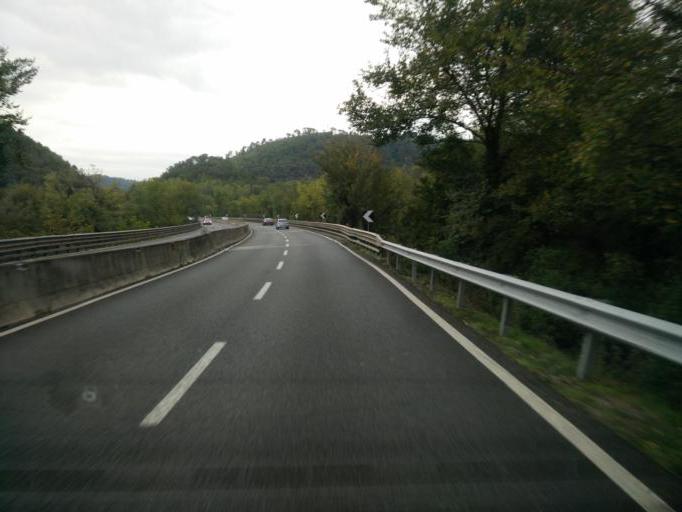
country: IT
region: Tuscany
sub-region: Province of Florence
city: Tavarnuzze
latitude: 43.6796
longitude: 11.2118
